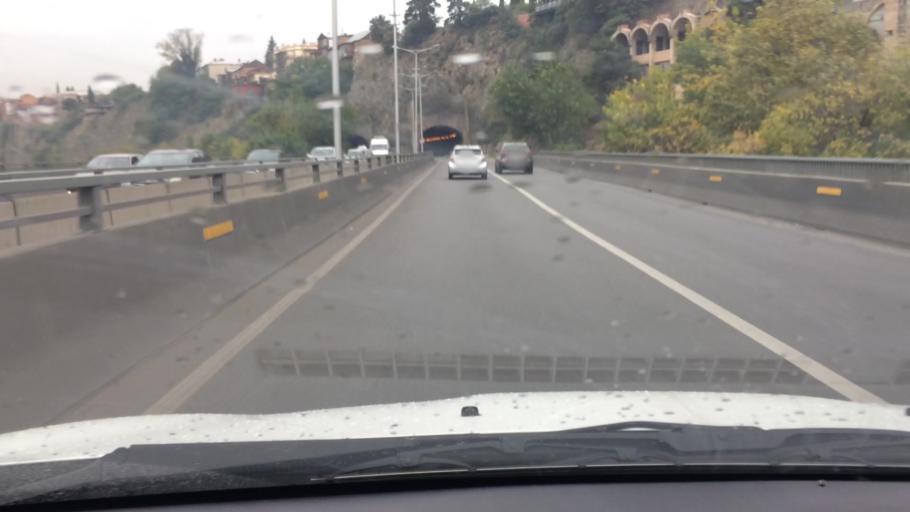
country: GE
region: T'bilisi
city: Tbilisi
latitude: 41.6872
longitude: 44.8219
